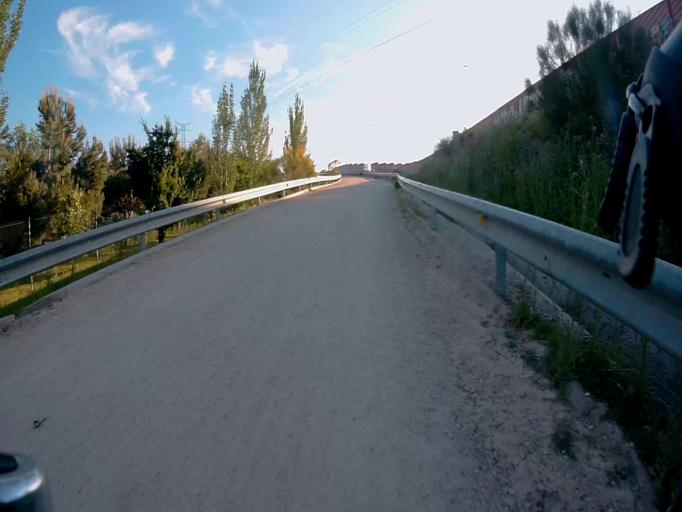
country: ES
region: Madrid
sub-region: Provincia de Madrid
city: Fuenlabrada
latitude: 40.3141
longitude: -3.7957
